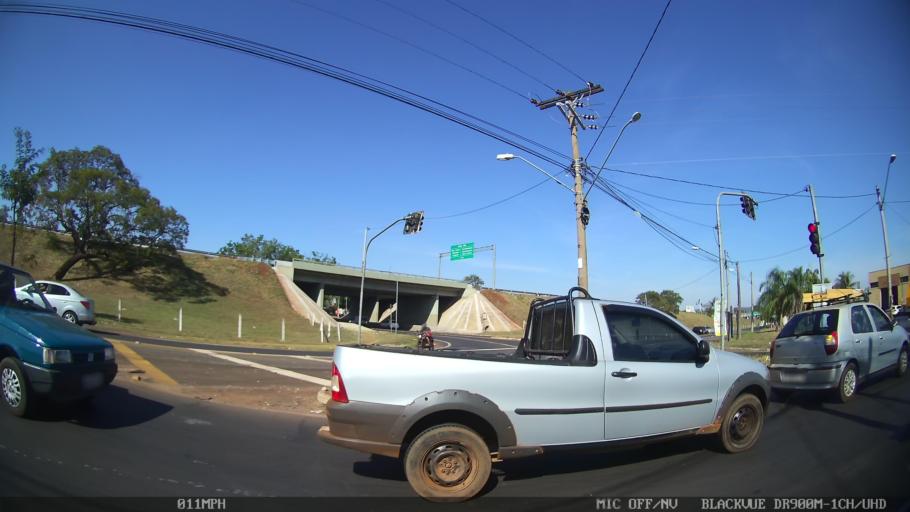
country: BR
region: Sao Paulo
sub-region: Ribeirao Preto
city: Ribeirao Preto
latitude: -21.1878
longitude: -47.7579
